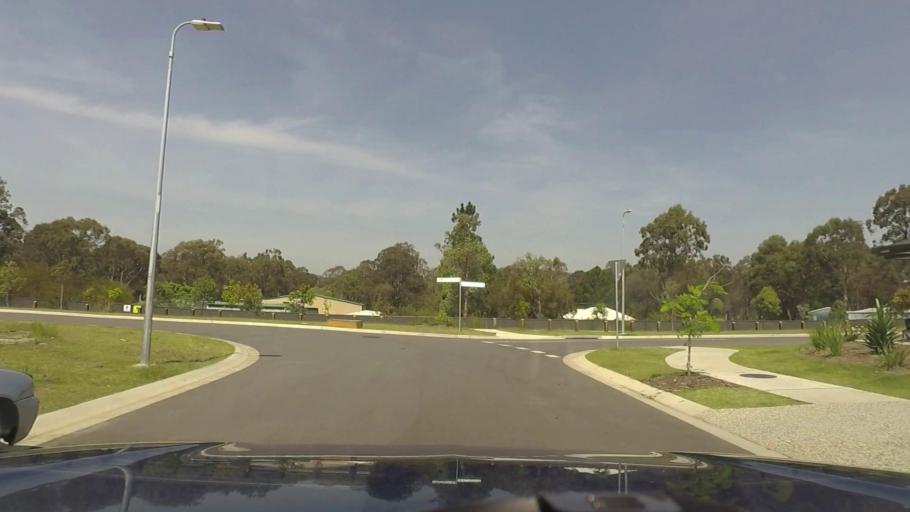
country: AU
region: Queensland
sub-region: Logan
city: Chambers Flat
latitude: -27.8005
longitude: 153.1207
